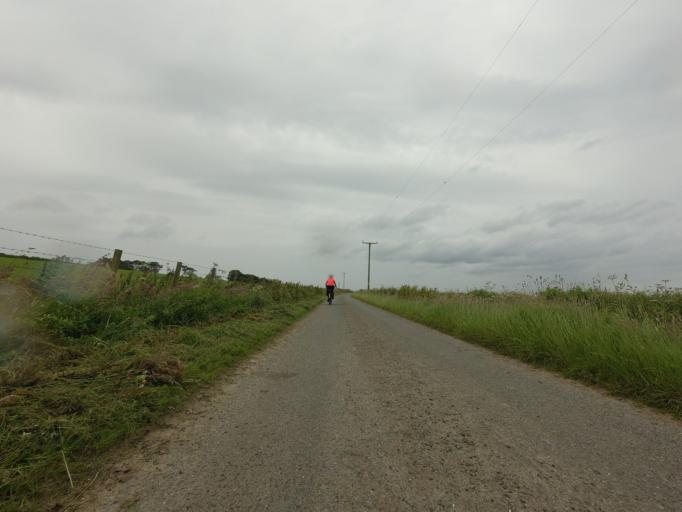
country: GB
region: Scotland
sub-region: Moray
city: Cullen
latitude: 57.6683
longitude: -2.7669
